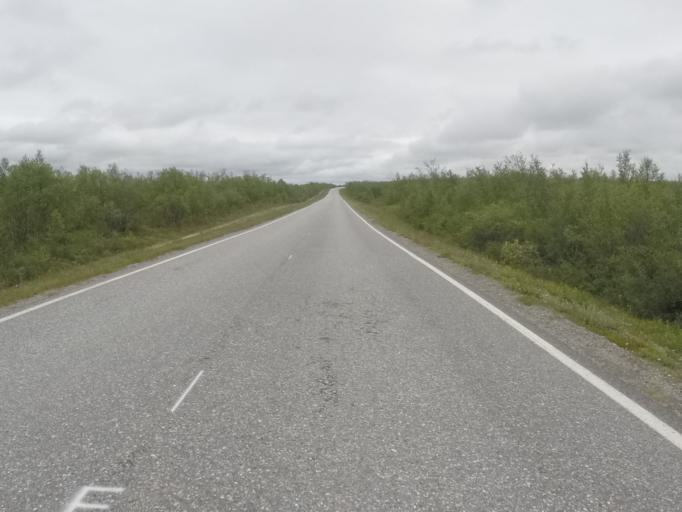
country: NO
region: Finnmark Fylke
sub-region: Kautokeino
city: Kautokeino
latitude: 69.0567
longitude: 23.1277
